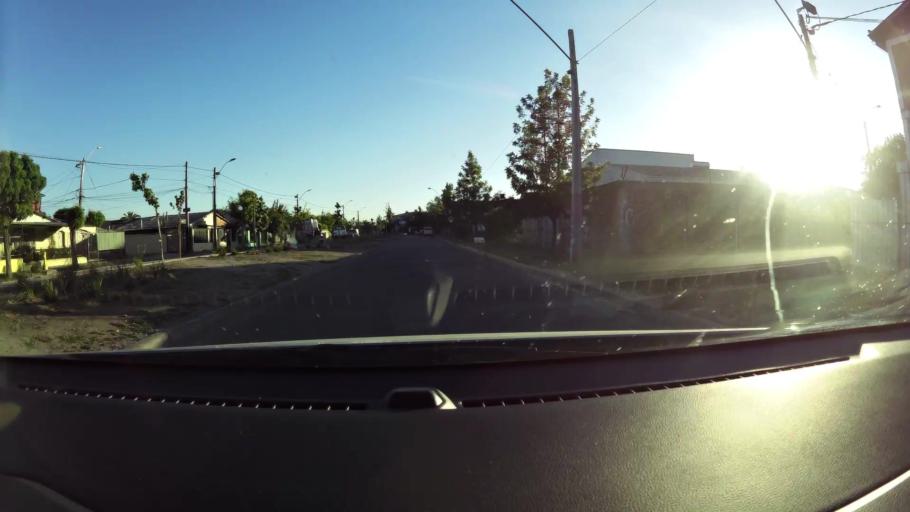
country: CL
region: Santiago Metropolitan
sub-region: Provincia de Maipo
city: San Bernardo
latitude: -33.5805
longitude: -70.6934
